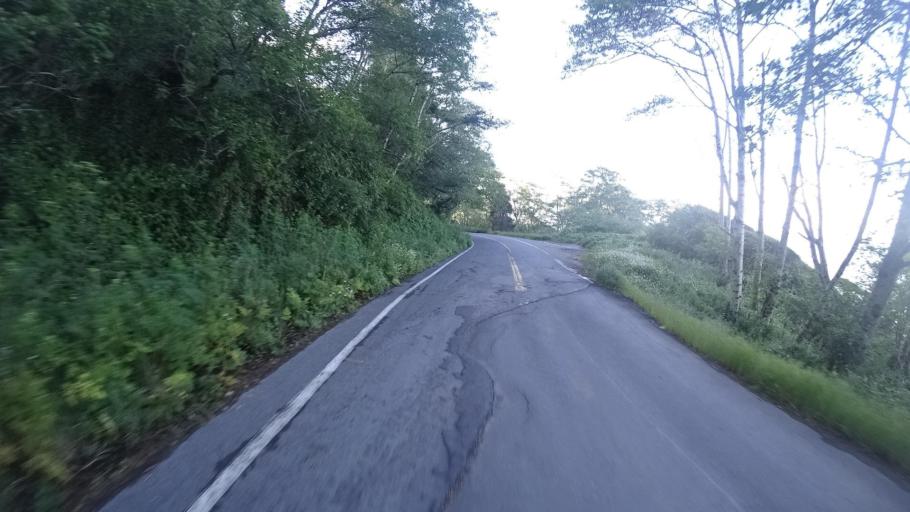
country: US
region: California
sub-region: Humboldt County
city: Westhaven-Moonstone
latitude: 41.1065
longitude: -124.1595
